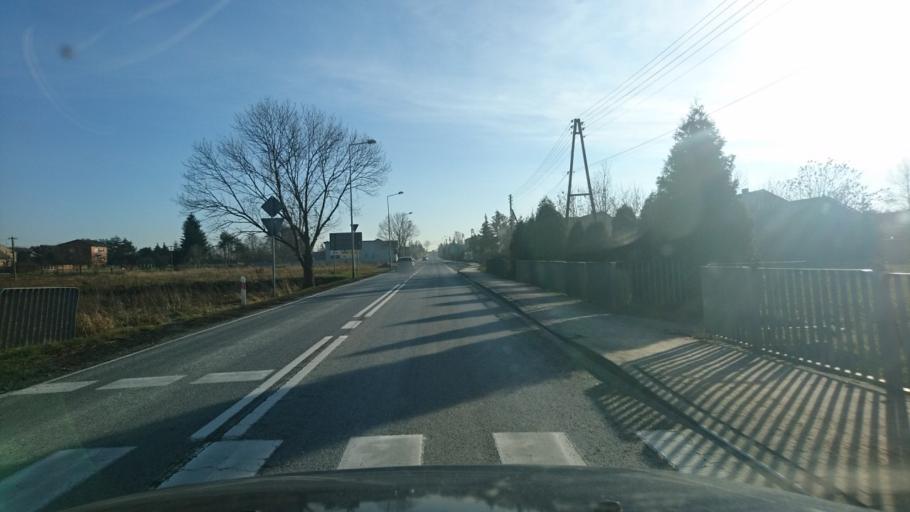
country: PL
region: Silesian Voivodeship
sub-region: Powiat klobucki
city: Starokrzepice
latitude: 51.0255
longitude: 18.6475
